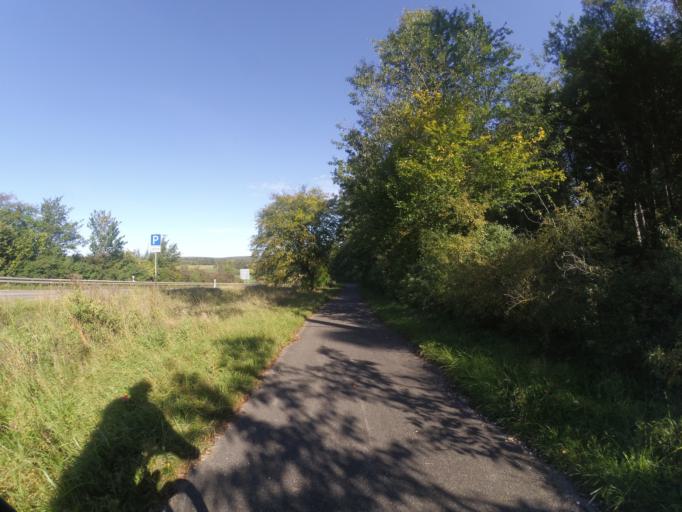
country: DE
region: Baden-Wuerttemberg
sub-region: Tuebingen Region
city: Breitingen
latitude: 48.5066
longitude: 9.9877
